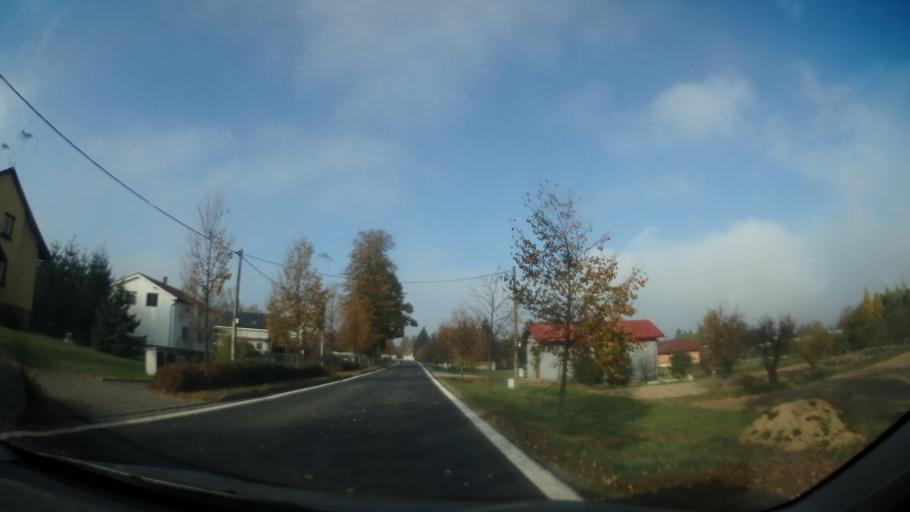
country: CZ
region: Vysocina
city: Krizanov
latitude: 49.4396
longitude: 16.1487
